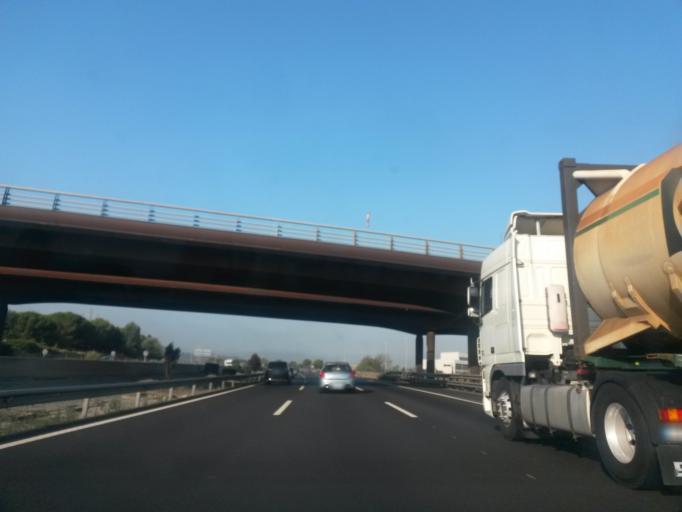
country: ES
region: Catalonia
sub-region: Provincia de Barcelona
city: Rubi
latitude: 41.4869
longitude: 2.0526
